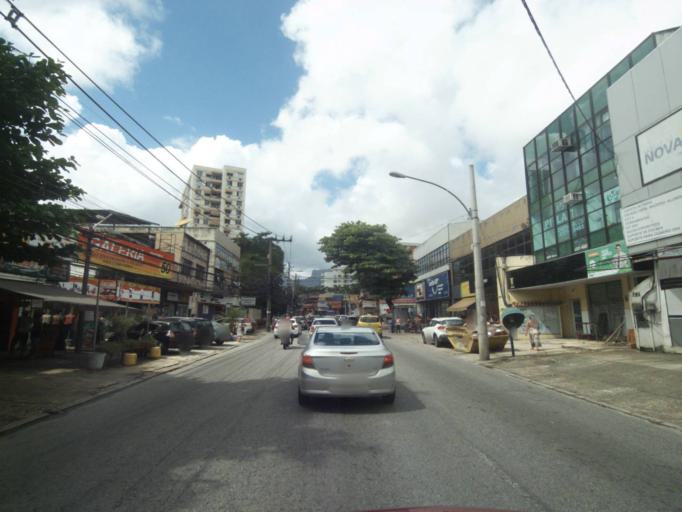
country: BR
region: Rio de Janeiro
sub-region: Sao Joao De Meriti
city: Sao Joao de Meriti
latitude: -22.9285
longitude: -43.3566
